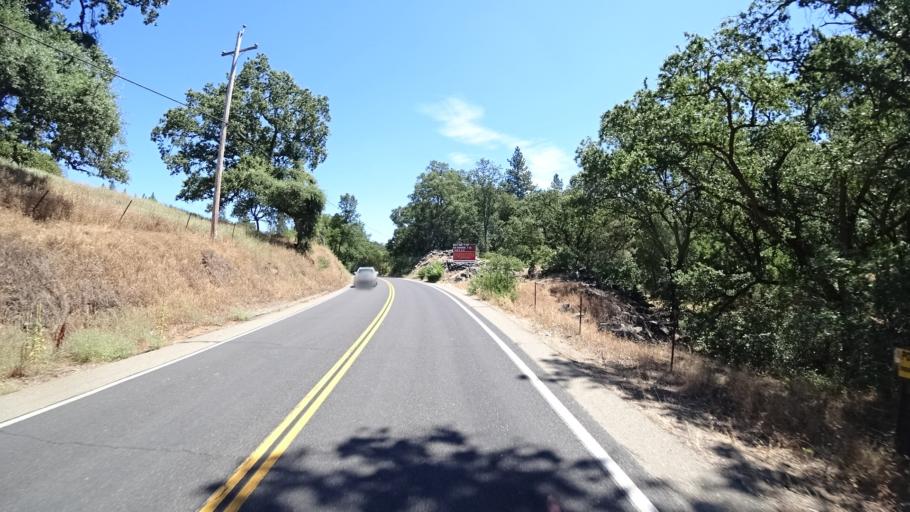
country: US
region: California
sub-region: Calaveras County
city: Murphys
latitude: 38.1367
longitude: -120.4705
